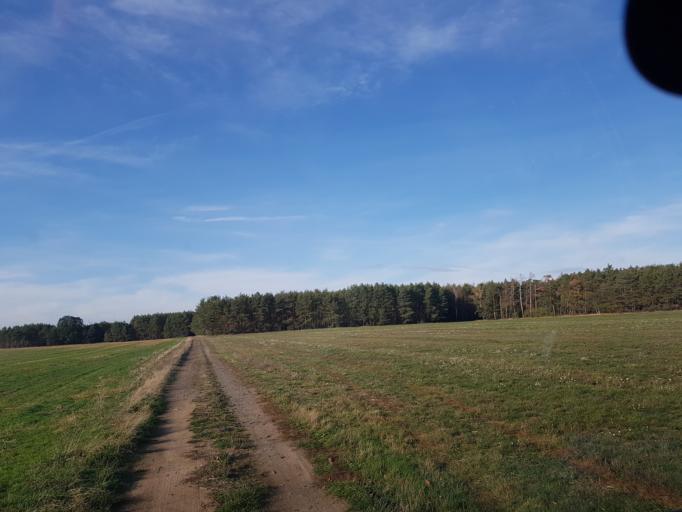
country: DE
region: Brandenburg
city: Bad Liebenwerda
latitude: 51.5391
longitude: 13.3422
